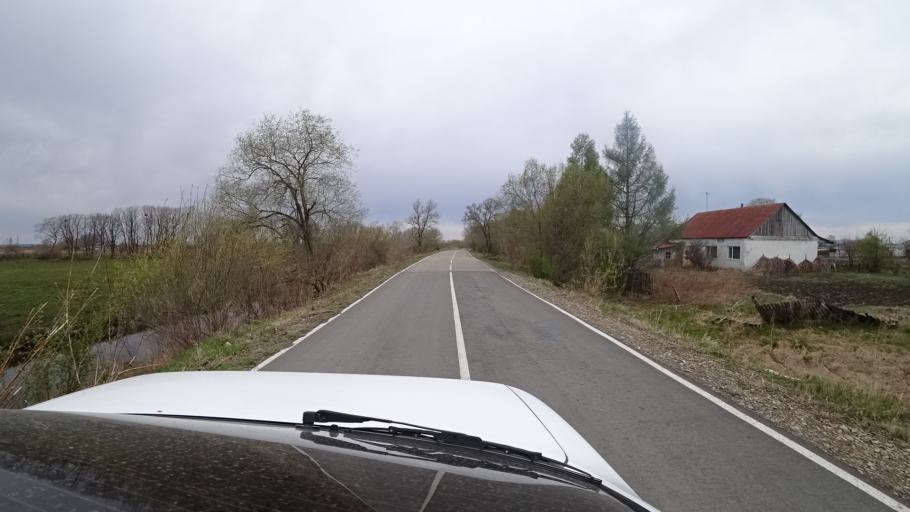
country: RU
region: Primorskiy
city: Dal'nerechensk
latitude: 45.9734
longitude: 133.7524
